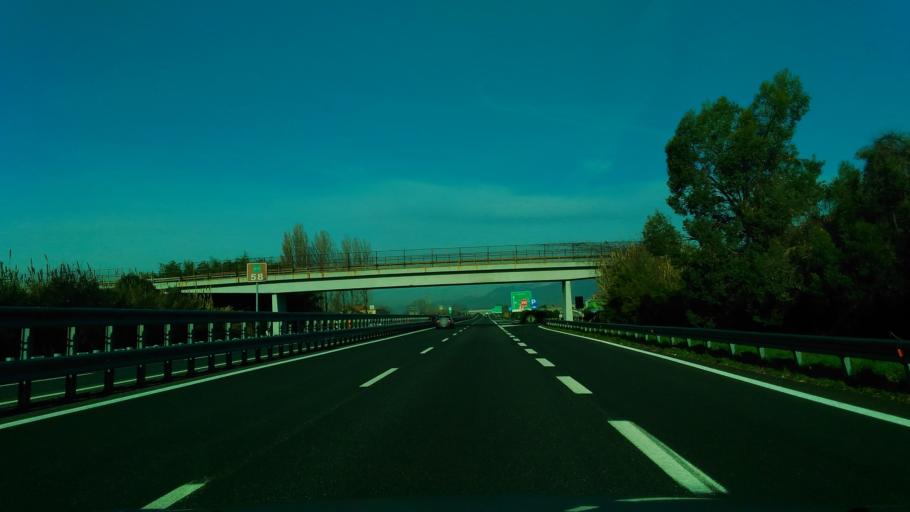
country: IT
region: Tuscany
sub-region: Provincia di Lucca
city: Viareggio
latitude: 43.8766
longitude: 10.2710
